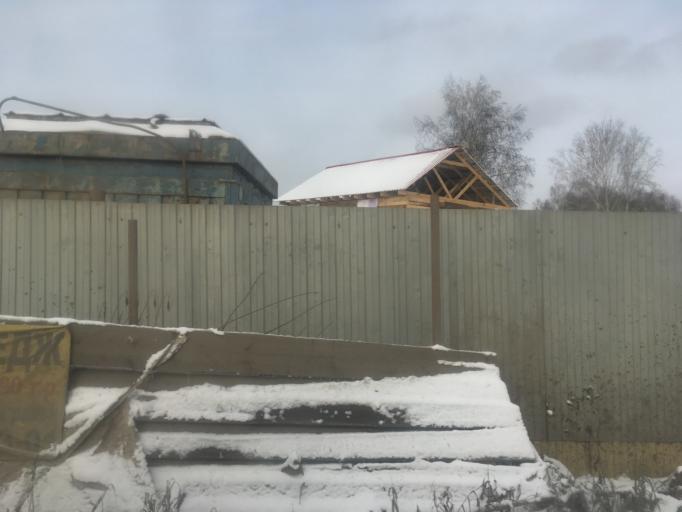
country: RU
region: Novosibirsk
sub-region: Novosibirskiy Rayon
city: Novosibirsk
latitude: 55.0751
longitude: 83.0258
